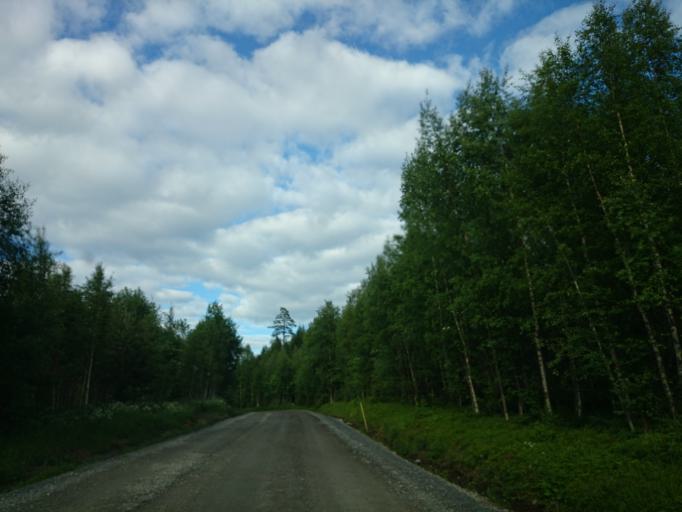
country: SE
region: Vaesternorrland
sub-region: Haernoesands Kommun
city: Haernoesand
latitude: 62.5852
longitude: 17.9449
